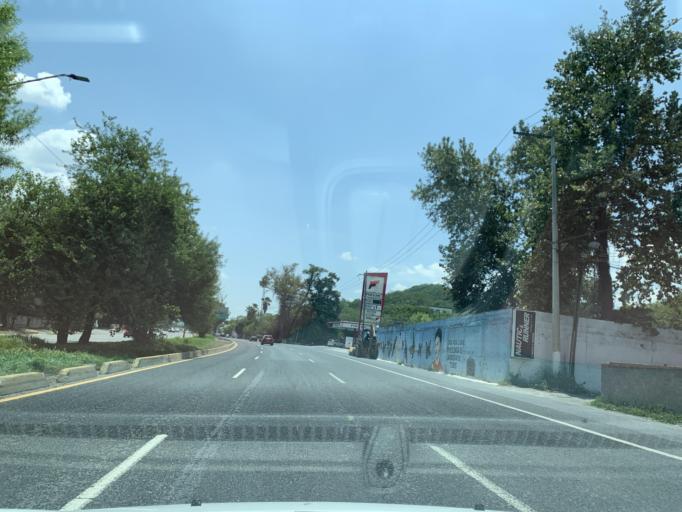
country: MX
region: Nuevo Leon
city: Santiago
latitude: 25.4237
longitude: -100.1474
